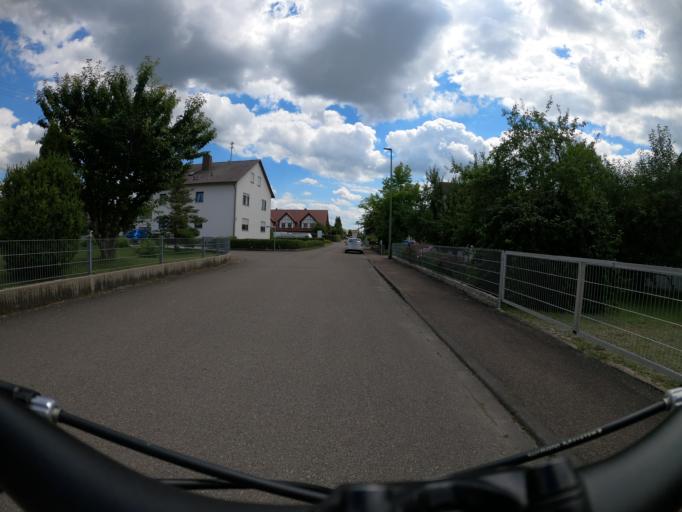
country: DE
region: Bavaria
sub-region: Swabia
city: Pfaffenhofen an der Roth
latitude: 48.3796
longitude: 10.1514
